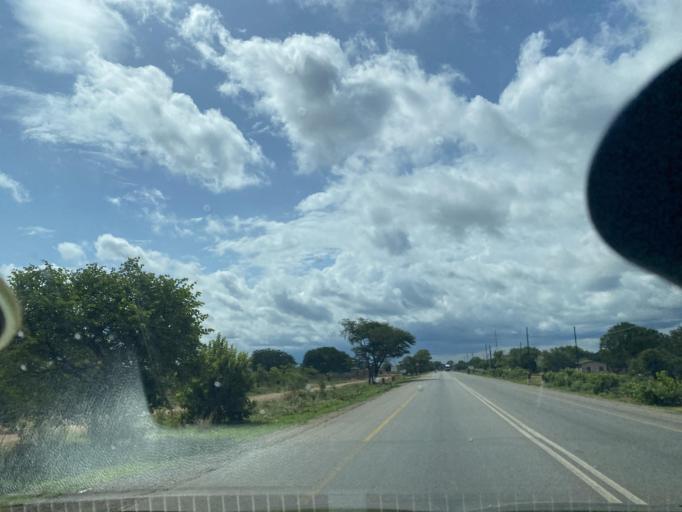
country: ZM
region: Lusaka
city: Kafue
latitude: -15.8563
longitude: 28.2580
